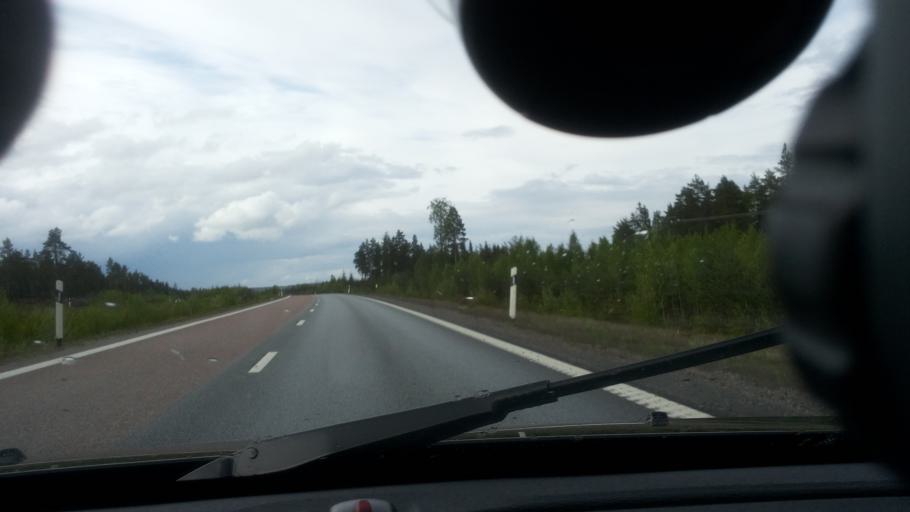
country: SE
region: Gaevleborg
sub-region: Soderhamns Kommun
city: Soderhamn
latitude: 61.3897
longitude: 16.9928
